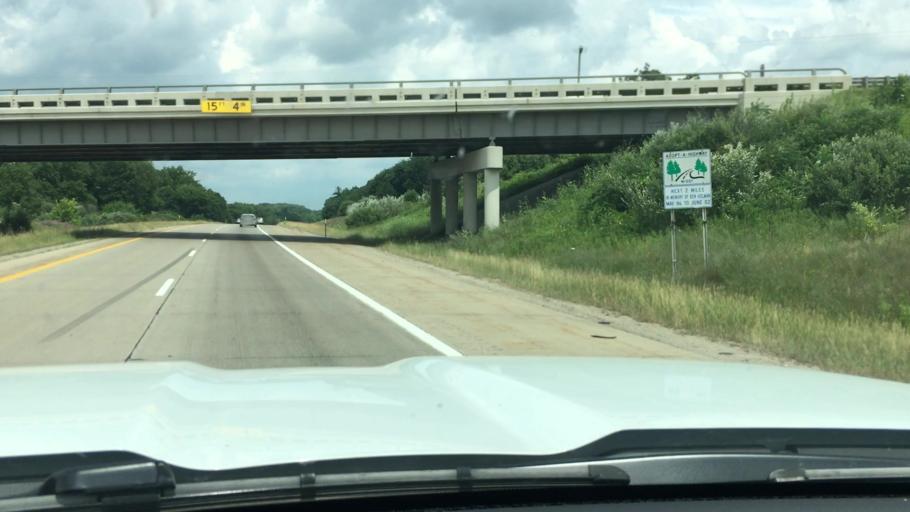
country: US
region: Michigan
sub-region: Kent County
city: Northview
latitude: 43.0887
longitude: -85.6319
